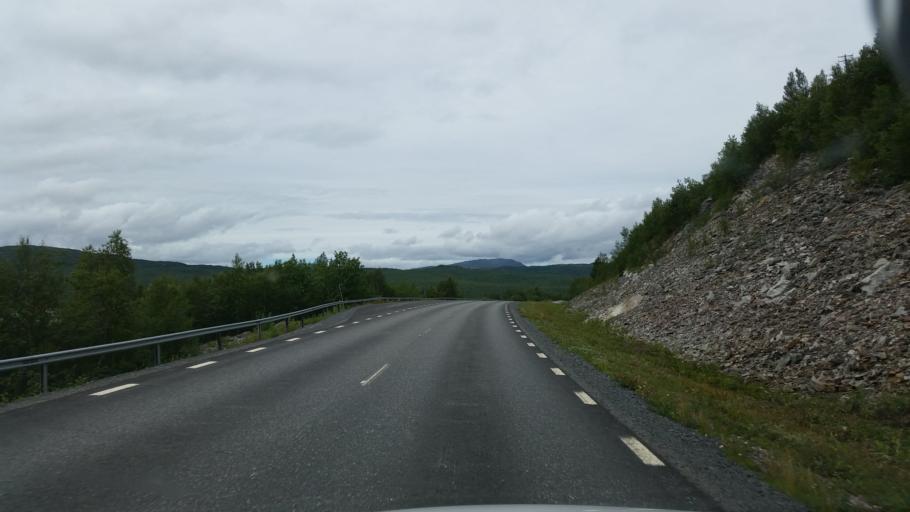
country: NO
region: Nordland
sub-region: Sorfold
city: Straumen
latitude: 66.5269
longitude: 16.3511
